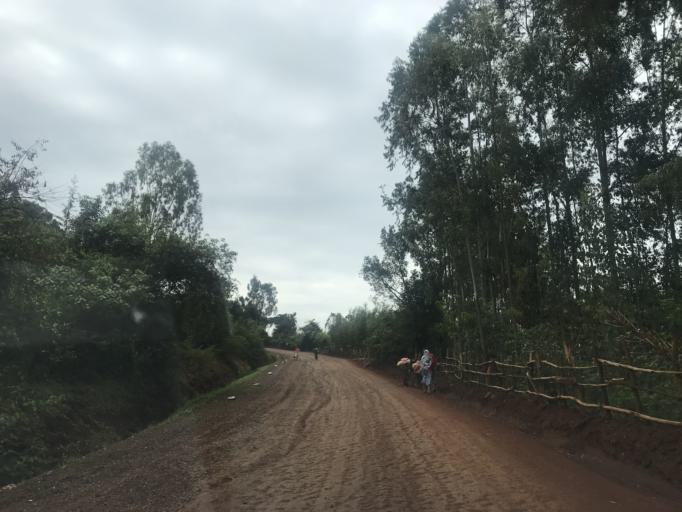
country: ET
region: Oromiya
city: Shambu
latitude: 9.8847
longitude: 36.6523
